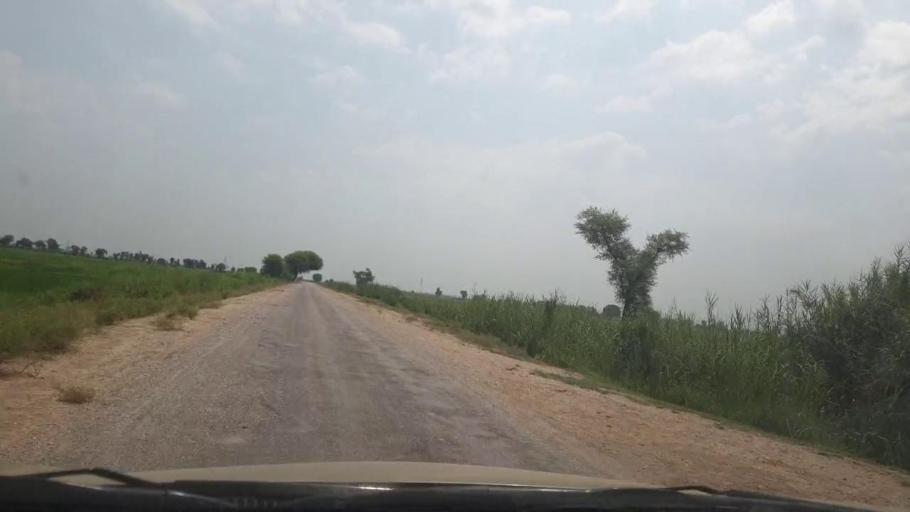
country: PK
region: Sindh
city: Ratodero
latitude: 27.7030
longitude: 68.2588
